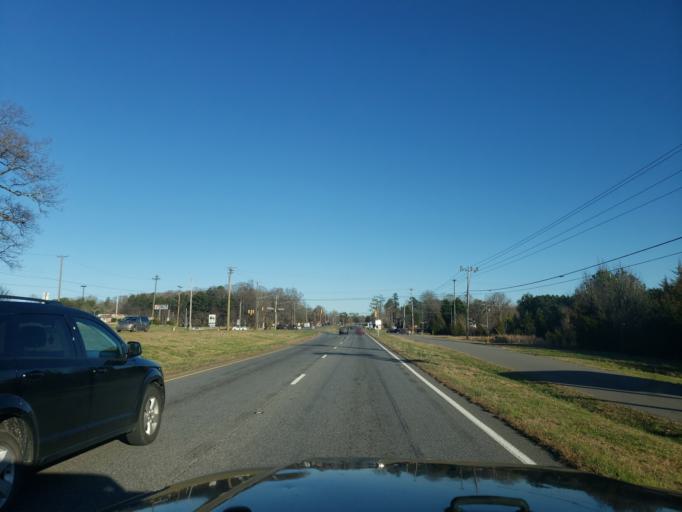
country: US
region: North Carolina
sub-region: Gaston County
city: Bessemer City
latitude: 35.2567
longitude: -81.2581
